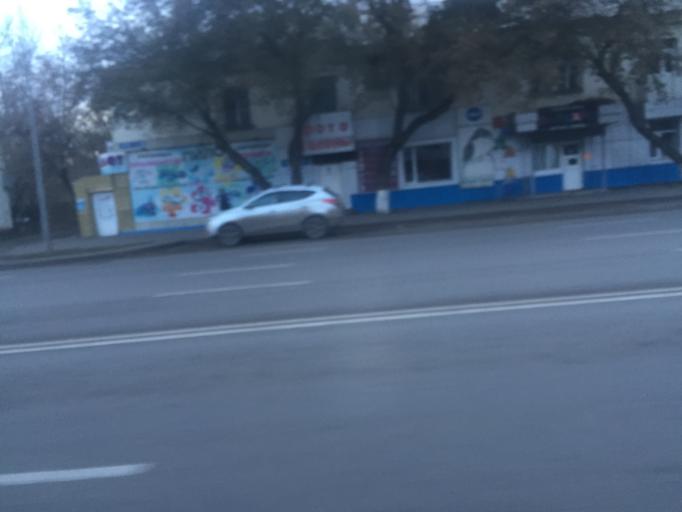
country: KZ
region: Astana Qalasy
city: Astana
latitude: 51.1740
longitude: 71.4115
